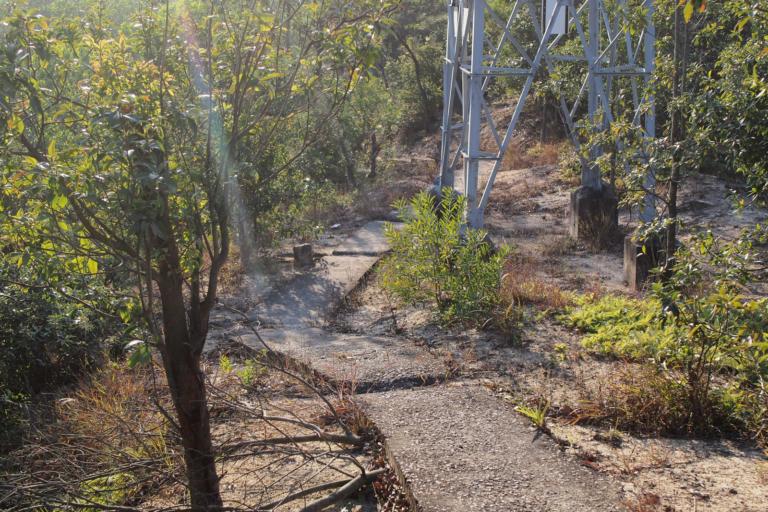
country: CN
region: Guangdong
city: Huancheng
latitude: 22.4428
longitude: 113.3987
